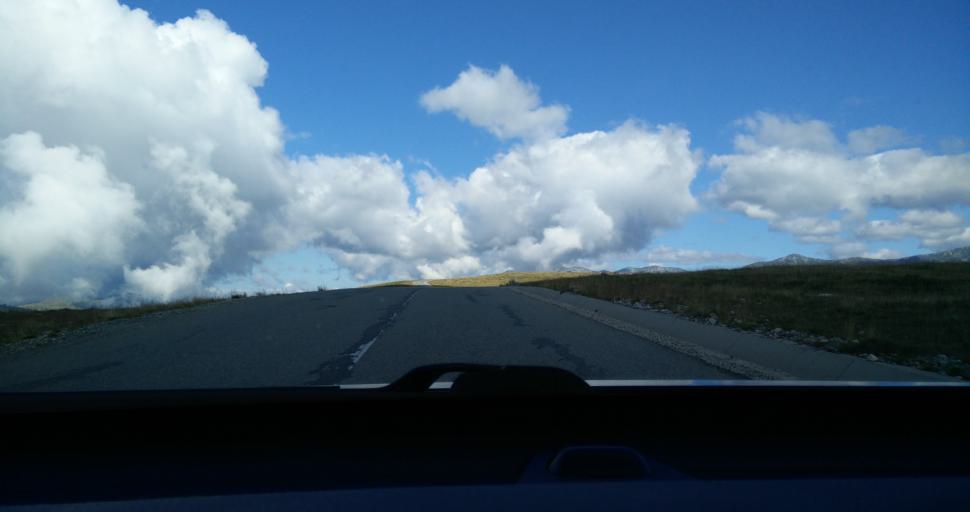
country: RO
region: Gorj
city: Novaci-Straini
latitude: 45.2606
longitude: 23.6924
